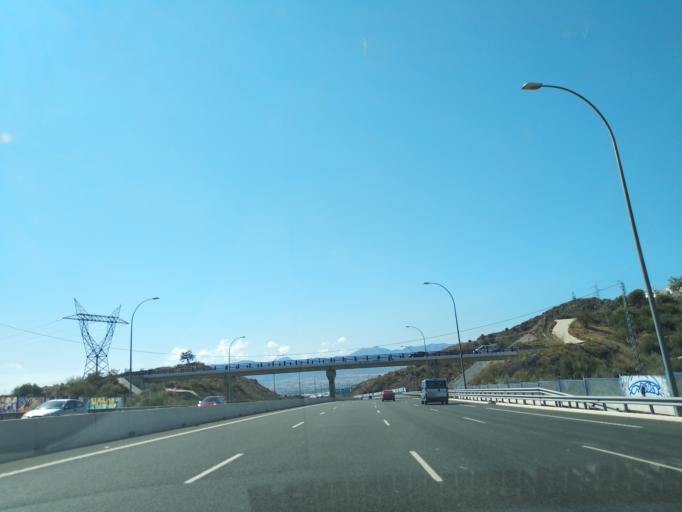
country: ES
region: Andalusia
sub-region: Provincia de Malaga
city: Malaga
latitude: 36.7388
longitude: -4.5041
